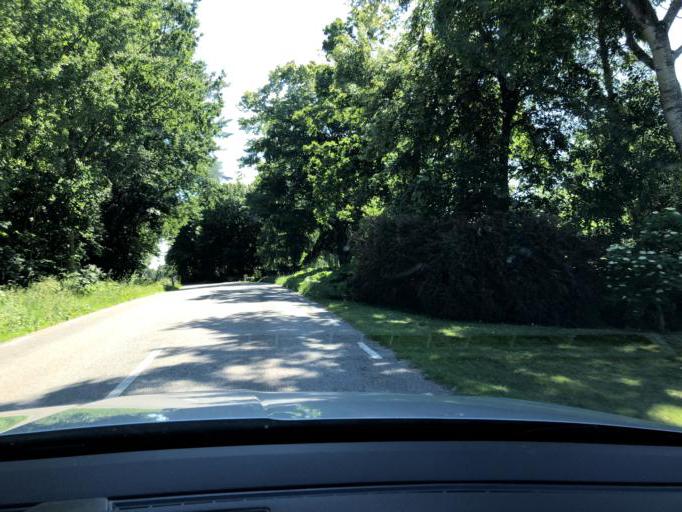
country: SE
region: Blekinge
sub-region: Solvesborgs Kommun
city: Soelvesborg
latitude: 56.1100
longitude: 14.6203
